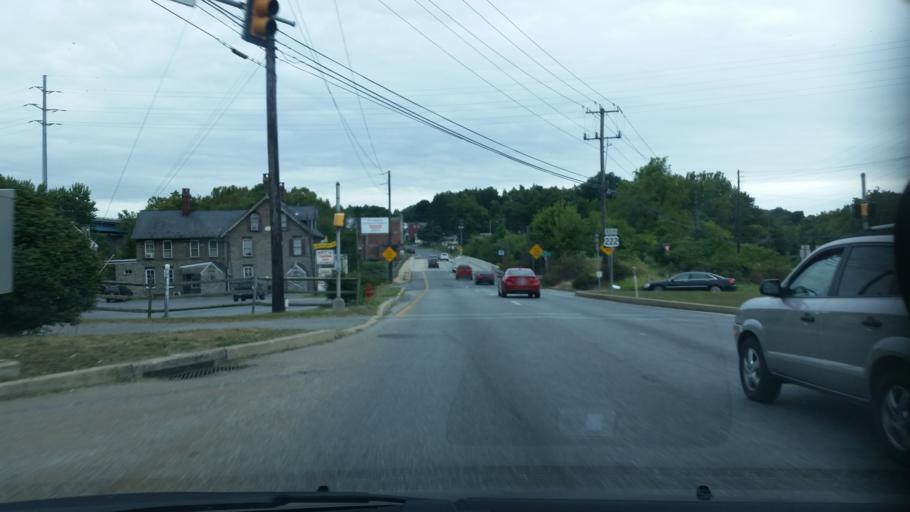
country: US
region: Pennsylvania
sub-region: Lancaster County
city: Lancaster
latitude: 40.0229
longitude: -76.3047
